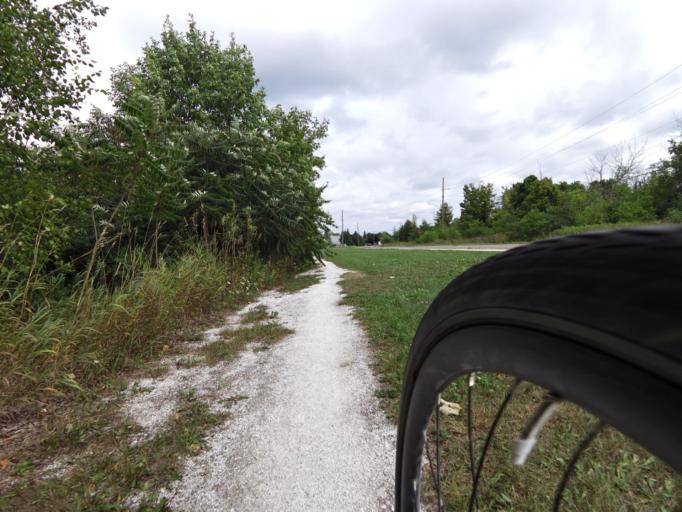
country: CA
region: Ontario
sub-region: Lanark County
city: Smiths Falls
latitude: 44.8902
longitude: -76.0263
